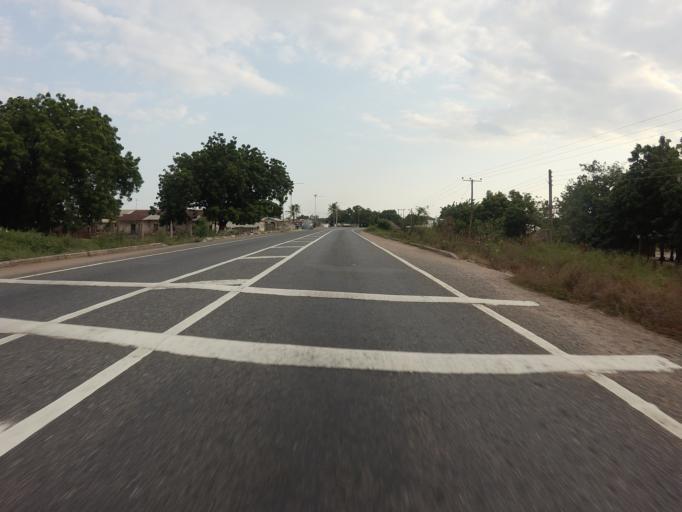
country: GH
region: Volta
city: Anloga
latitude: 6.1056
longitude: 0.5146
